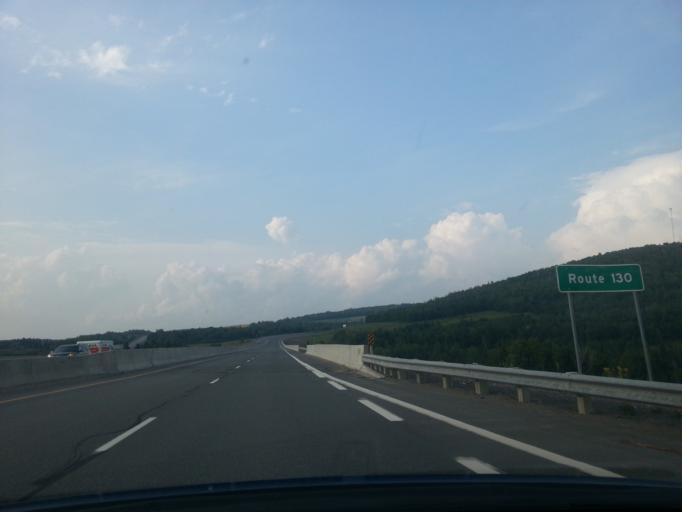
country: US
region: Maine
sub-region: Aroostook County
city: Fort Fairfield
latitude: 46.8196
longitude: -67.7332
